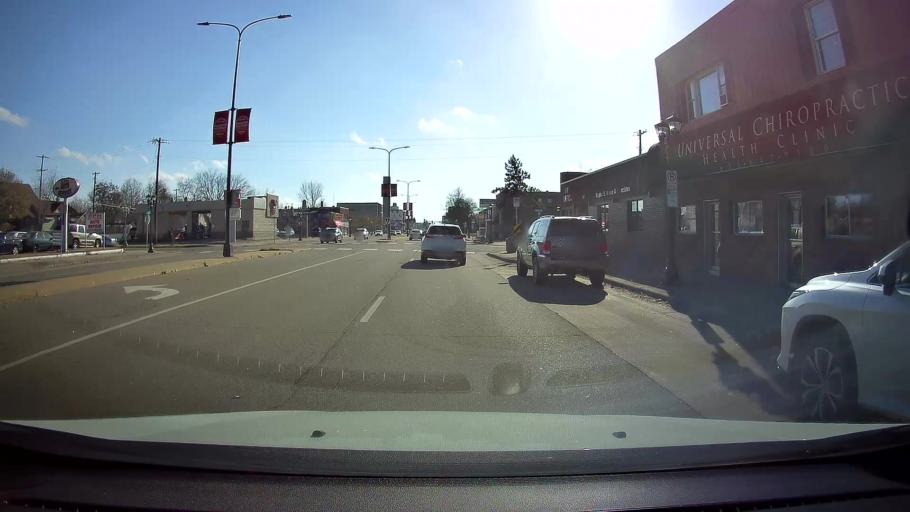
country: US
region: Minnesota
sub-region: Ramsey County
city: Falcon Heights
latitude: 44.9615
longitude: -93.1672
